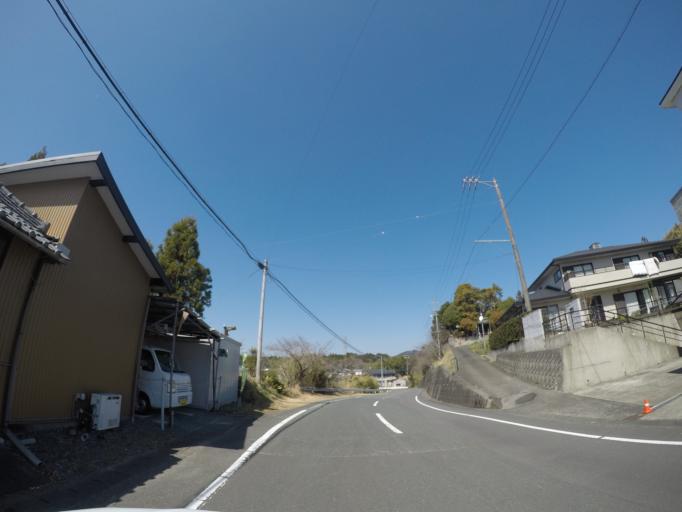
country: JP
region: Shizuoka
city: Kanaya
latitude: 34.7803
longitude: 138.1100
